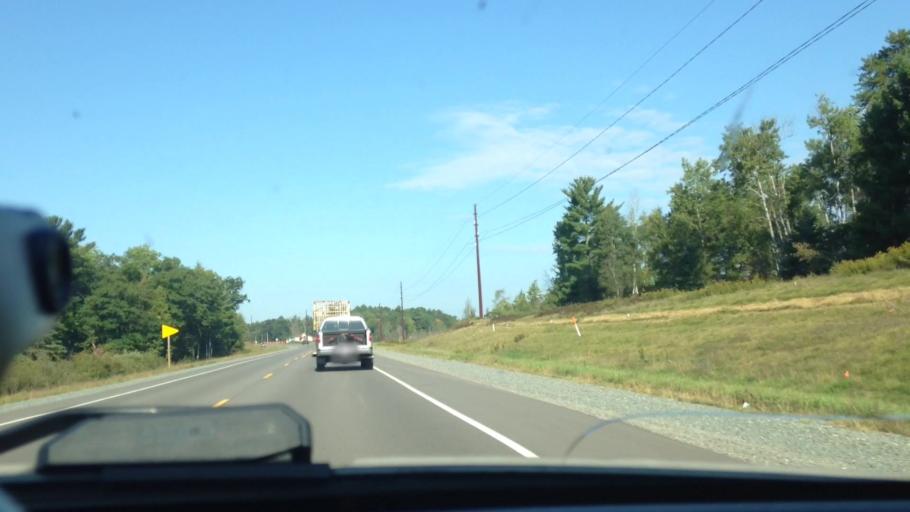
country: US
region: Michigan
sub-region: Dickinson County
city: Iron Mountain
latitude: 45.8786
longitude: -88.1214
